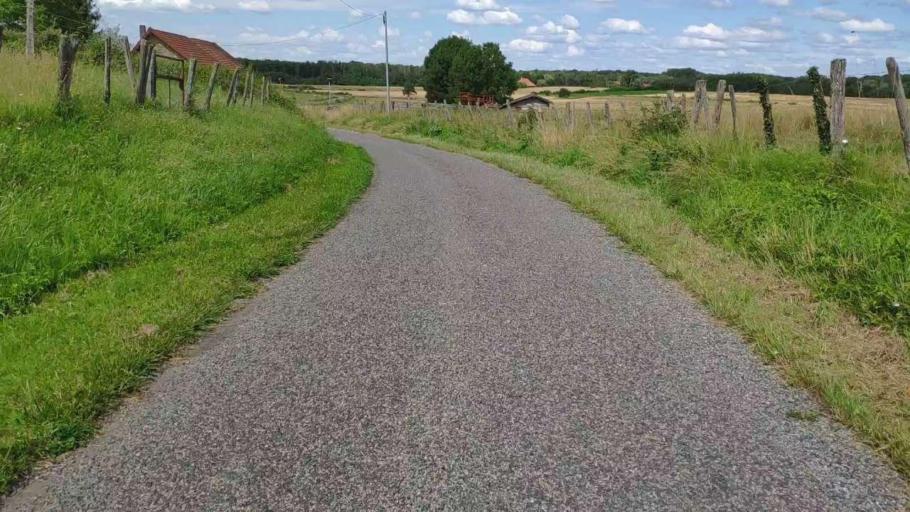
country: FR
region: Franche-Comte
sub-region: Departement du Jura
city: Bletterans
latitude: 46.8234
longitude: 5.4518
